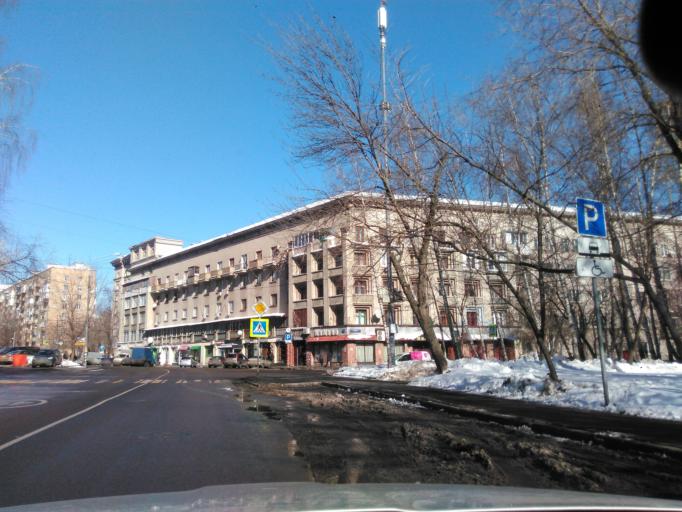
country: RU
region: Moskovskaya
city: Dorogomilovo
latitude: 55.7969
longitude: 37.5687
